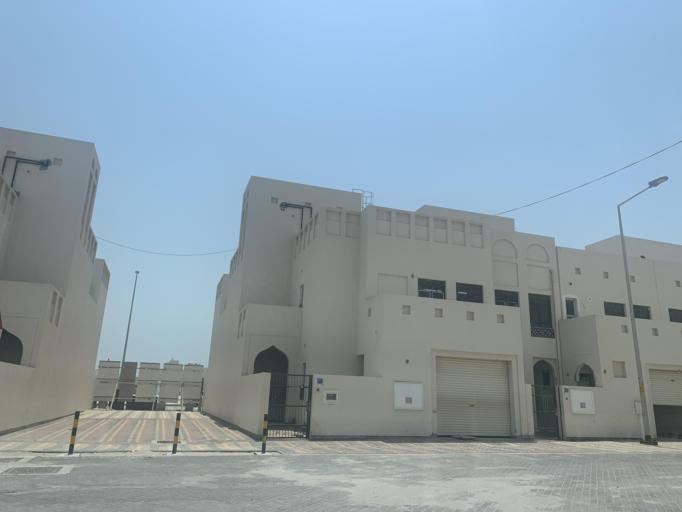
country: BH
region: Muharraq
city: Al Hadd
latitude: 26.2374
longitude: 50.6697
